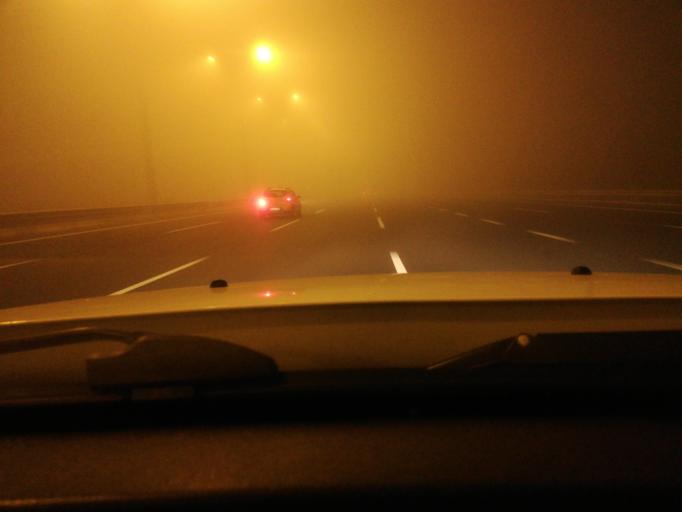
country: TR
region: Istanbul
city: Sultanbeyli
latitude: 40.9806
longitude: 29.3280
